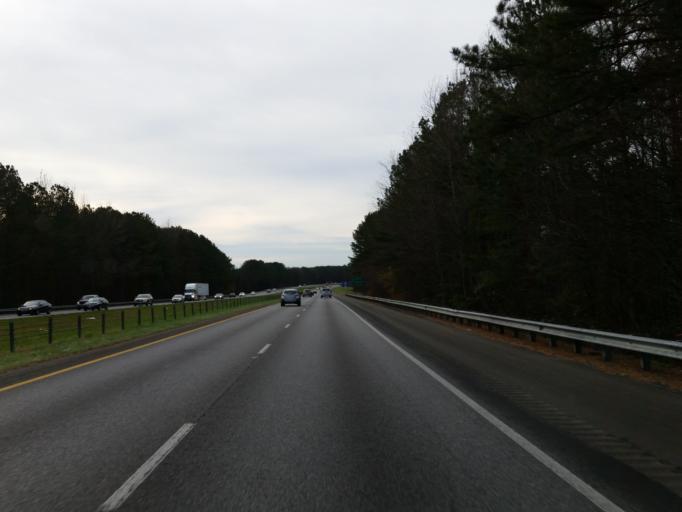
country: US
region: Georgia
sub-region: Cherokee County
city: Holly Springs
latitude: 34.1667
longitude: -84.5124
